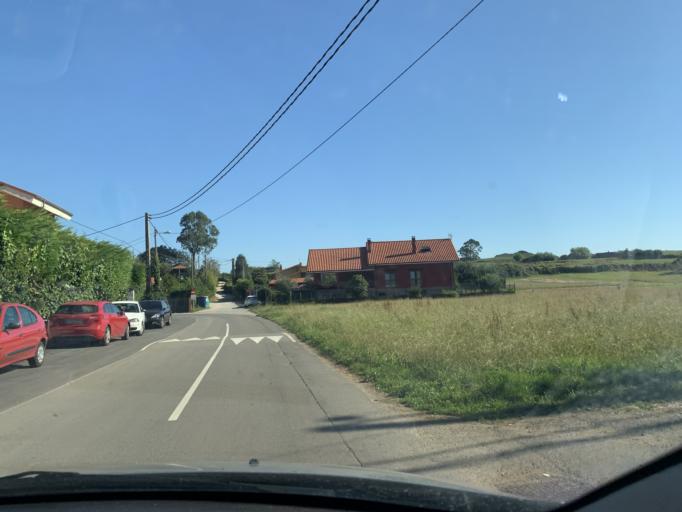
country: ES
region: Asturias
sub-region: Province of Asturias
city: Llanes
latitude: 43.4253
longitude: -4.7800
